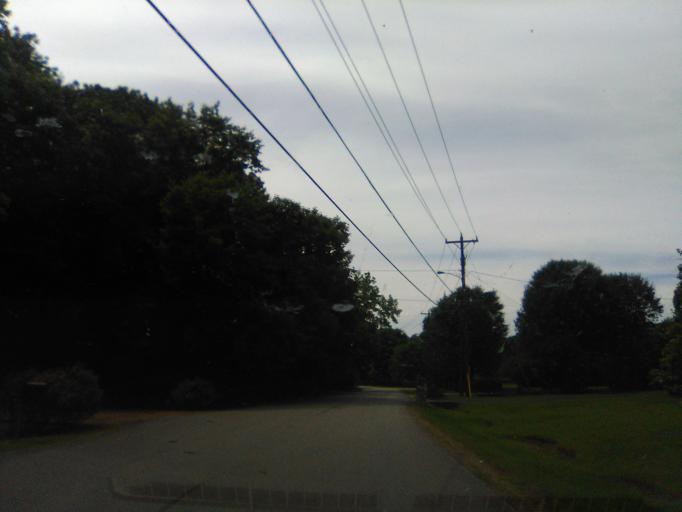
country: US
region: Tennessee
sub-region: Davidson County
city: Belle Meade
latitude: 36.1139
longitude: -86.9032
